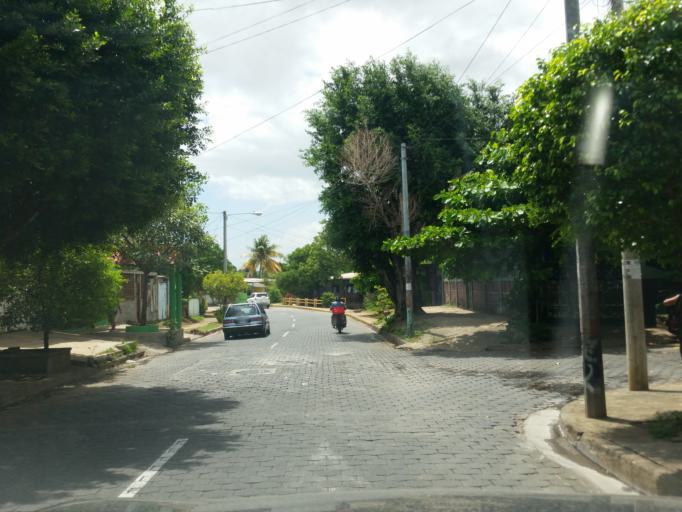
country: NI
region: Managua
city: Managua
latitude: 12.1274
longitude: -86.2484
